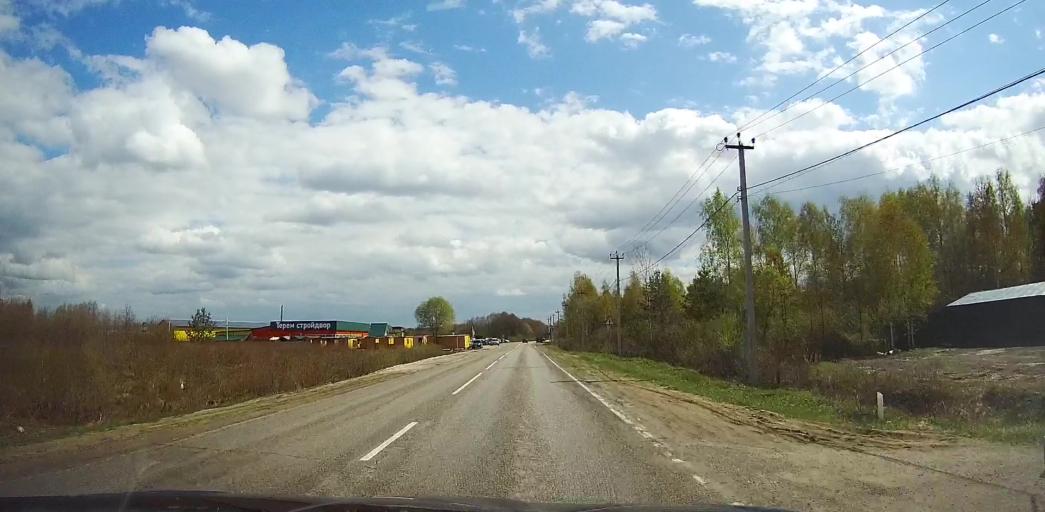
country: RU
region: Moskovskaya
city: Davydovo
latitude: 55.5497
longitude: 38.8028
